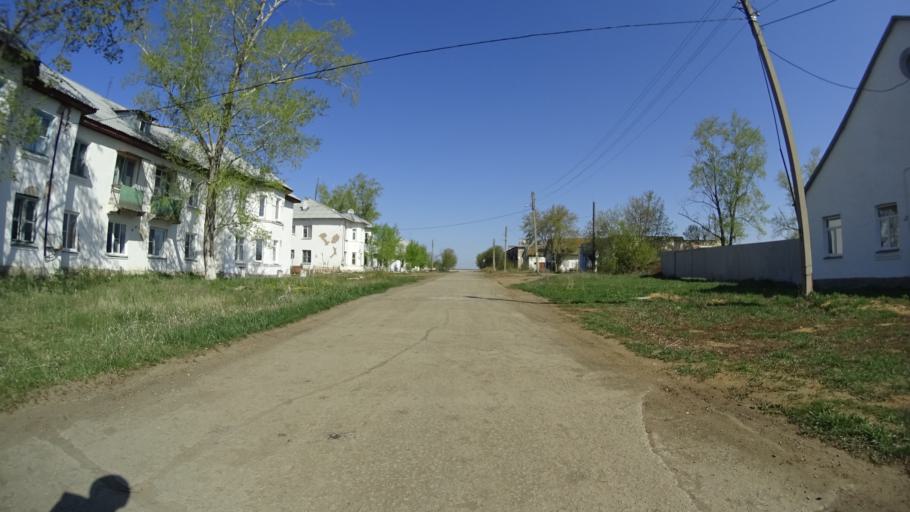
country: RU
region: Chelyabinsk
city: Troitsk
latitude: 54.1891
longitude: 61.5062
